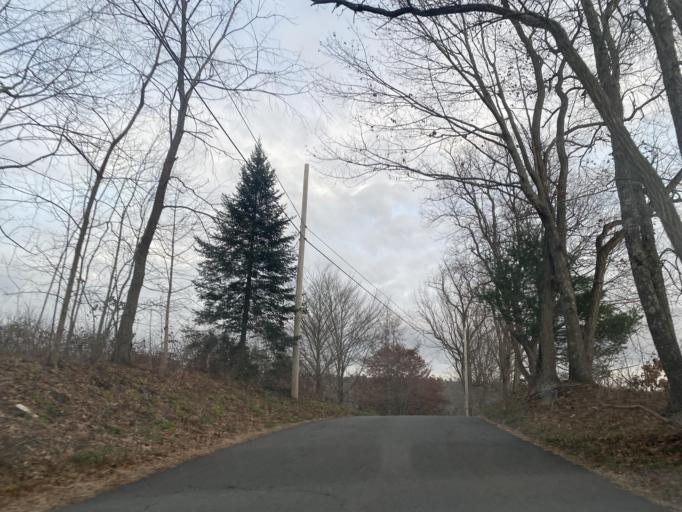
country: US
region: Massachusetts
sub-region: Worcester County
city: Spencer
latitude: 42.2617
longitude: -71.9524
